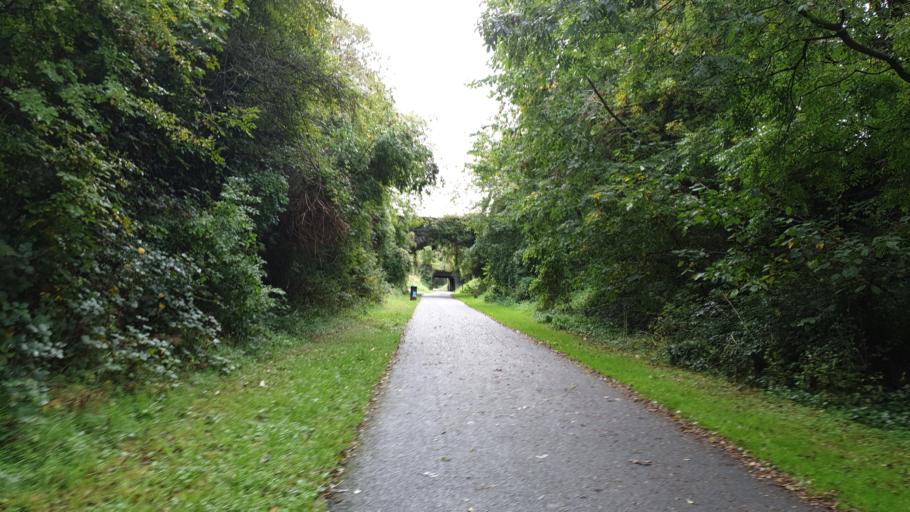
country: IE
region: Munster
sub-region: County Cork
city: Cork
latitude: 51.8913
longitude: -8.4129
